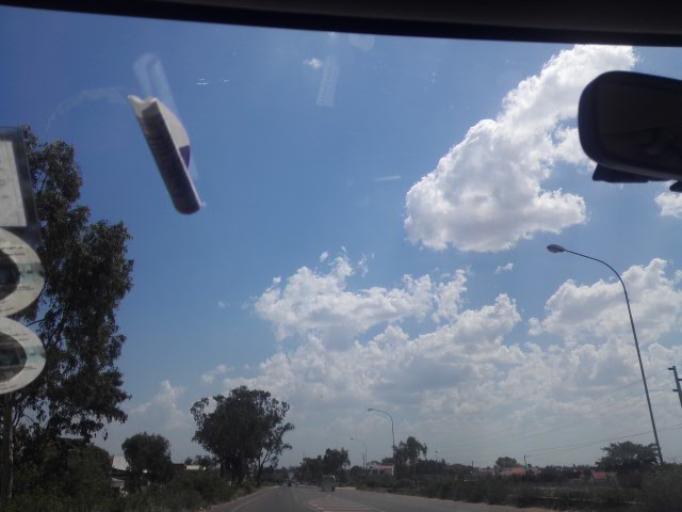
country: MZ
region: Maputo
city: Matola
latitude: -25.9665
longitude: 32.4448
